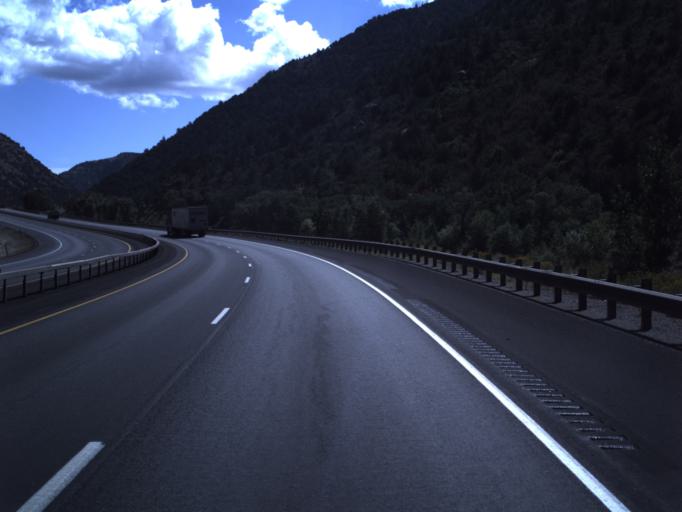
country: US
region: Utah
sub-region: Sevier County
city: Salina
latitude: 38.8962
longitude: -111.6286
